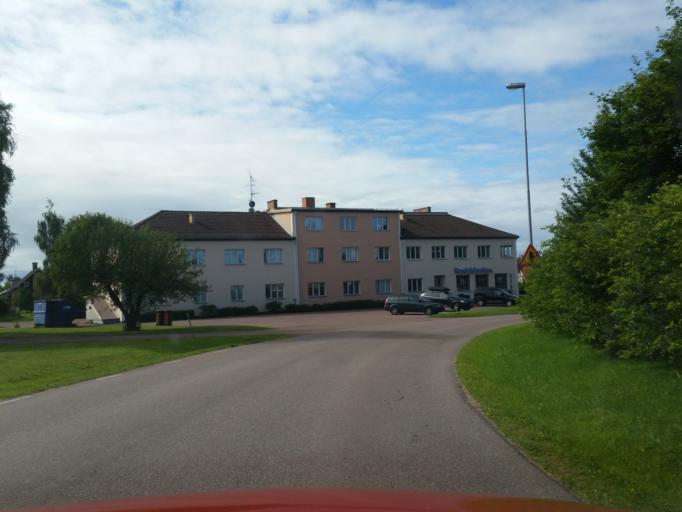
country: SE
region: Dalarna
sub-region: Leksand Municipality
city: Smedby
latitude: 60.6785
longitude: 15.0966
